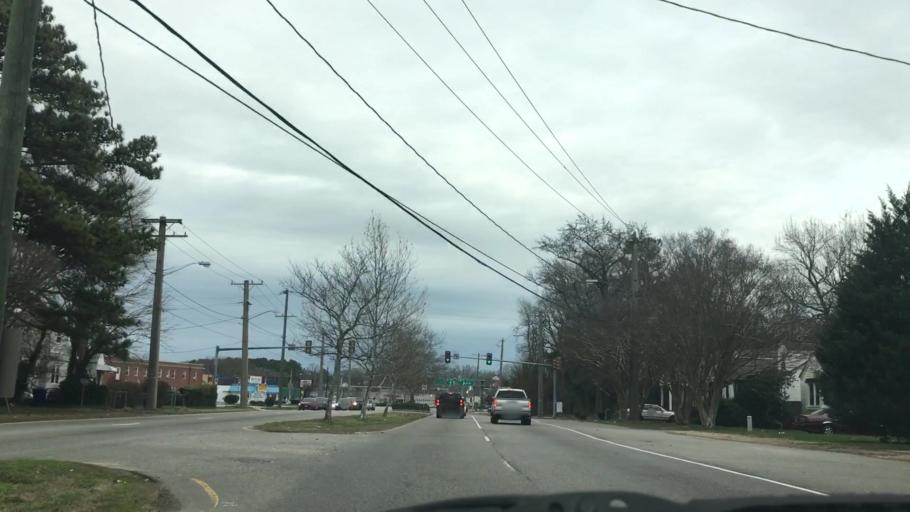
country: US
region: Virginia
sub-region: City of Norfolk
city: Norfolk
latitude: 36.8882
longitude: -76.2410
